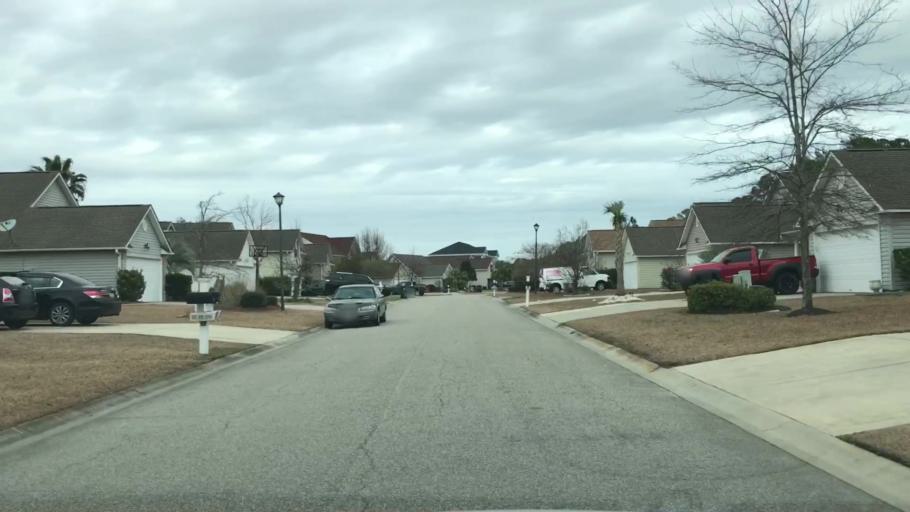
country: US
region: South Carolina
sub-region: Horry County
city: Socastee
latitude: 33.6708
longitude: -78.9722
